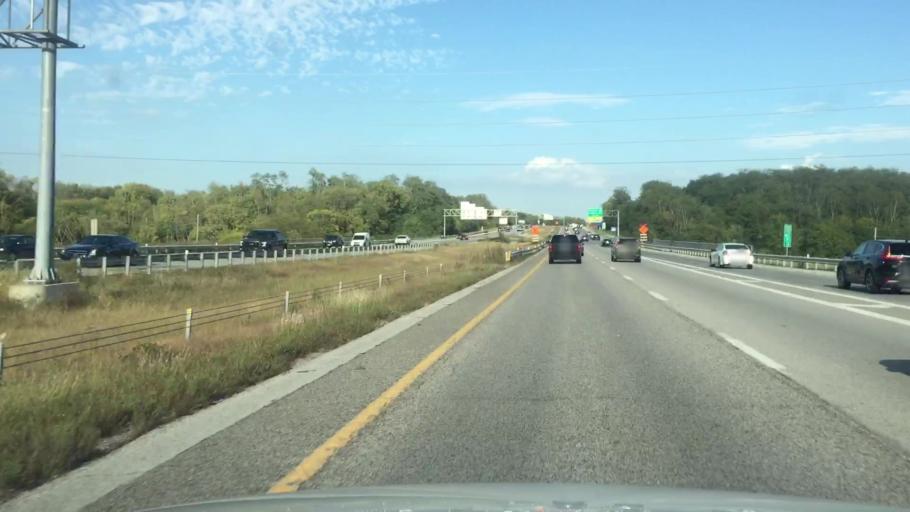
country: US
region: Missouri
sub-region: Jackson County
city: Lees Summit
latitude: 38.9385
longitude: -94.3967
